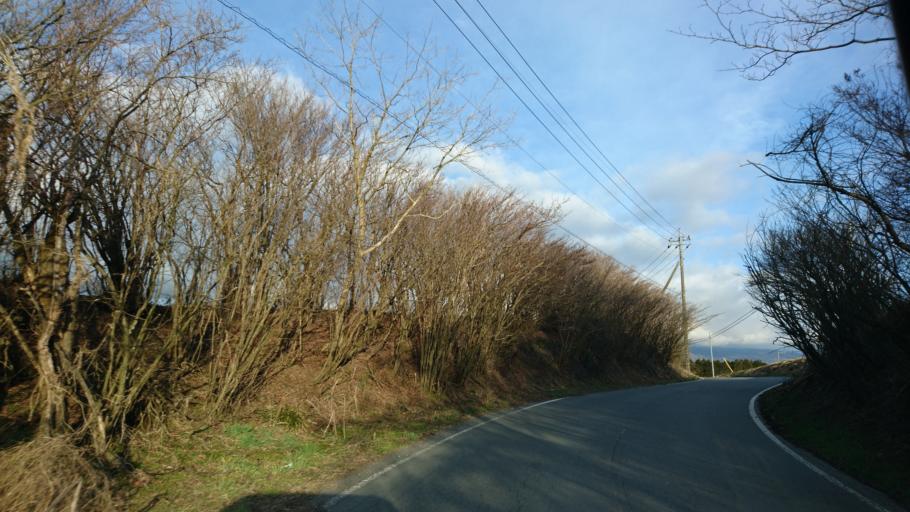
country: JP
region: Yamanashi
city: Fujikawaguchiko
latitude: 35.3902
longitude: 138.5937
